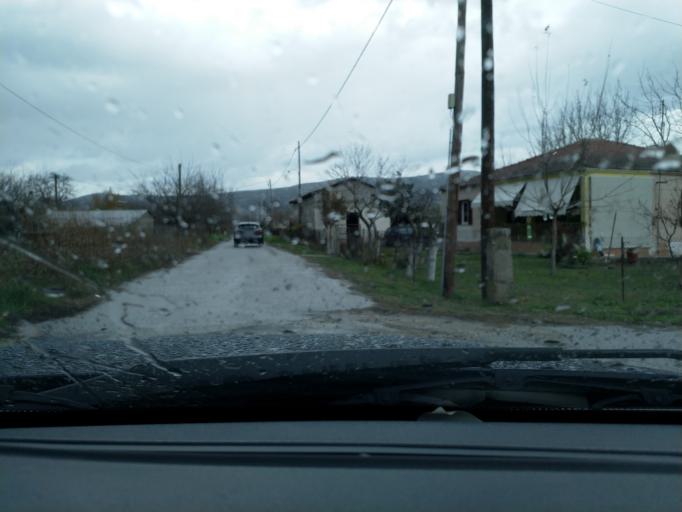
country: GR
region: Thessaly
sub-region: Trikala
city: Taxiarches
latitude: 39.5482
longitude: 21.8957
